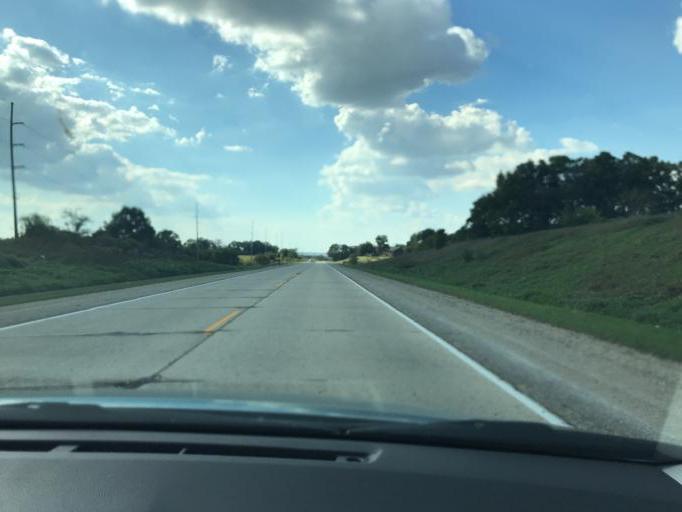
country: US
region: Wisconsin
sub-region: Green County
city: Brodhead
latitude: 42.5589
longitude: -89.3106
